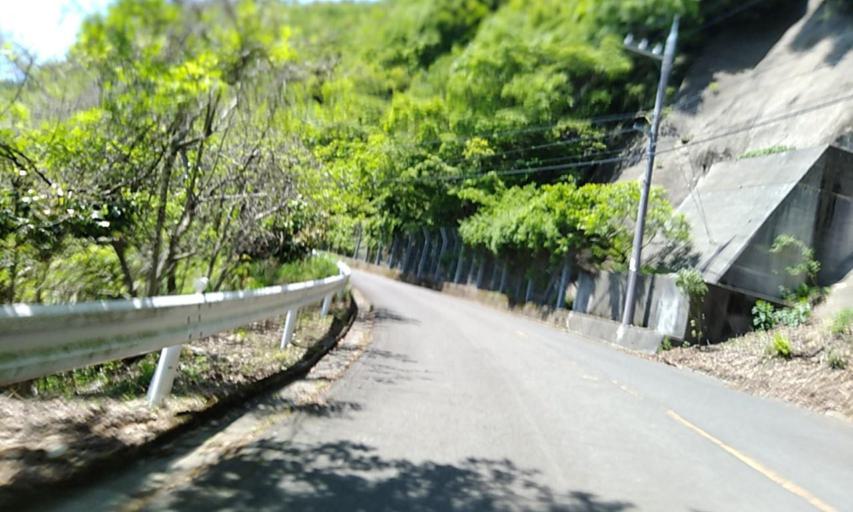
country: JP
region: Fukui
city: Obama
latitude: 35.5453
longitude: 135.7466
